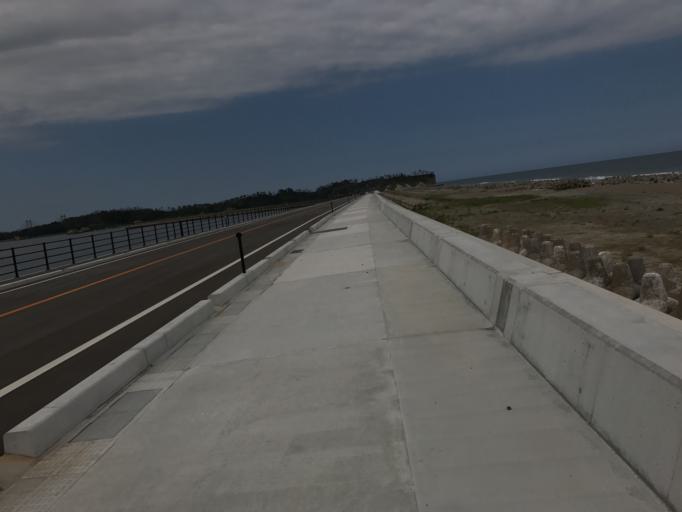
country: JP
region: Miyagi
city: Marumori
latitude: 37.8122
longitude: 140.9855
